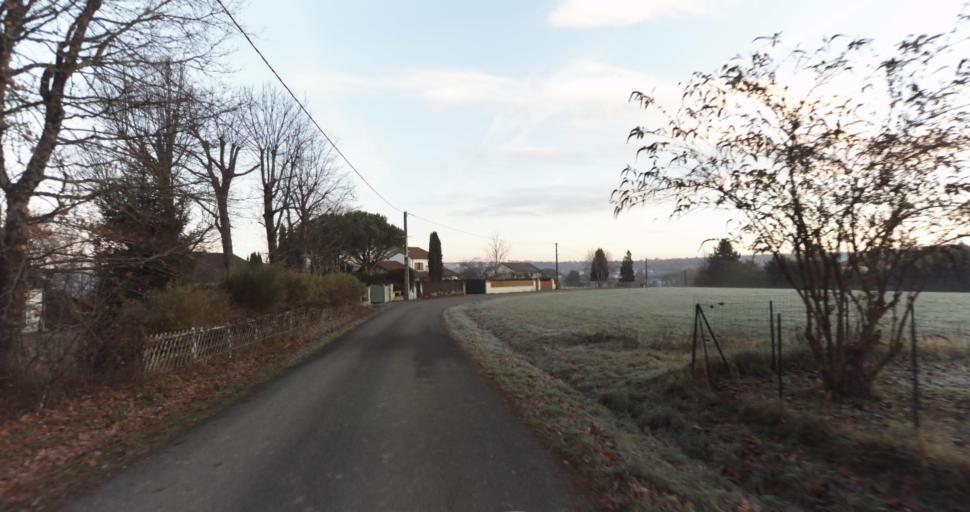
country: FR
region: Limousin
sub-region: Departement de la Haute-Vienne
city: Aixe-sur-Vienne
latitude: 45.8179
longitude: 1.1618
